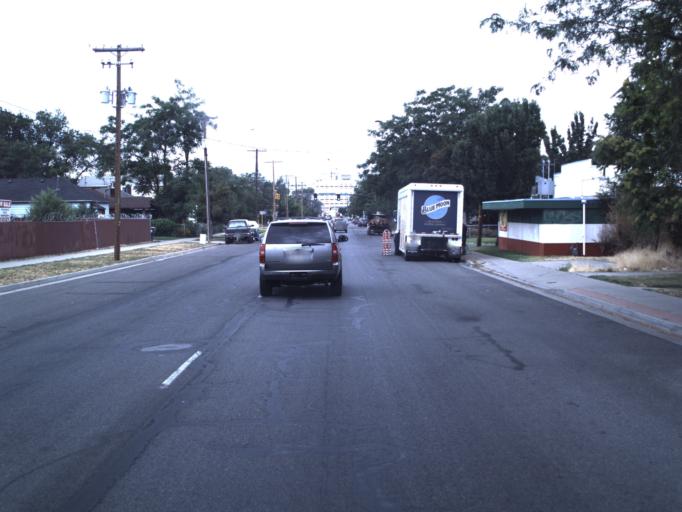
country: US
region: Utah
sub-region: Weber County
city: Ogden
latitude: 41.2103
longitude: -111.9716
